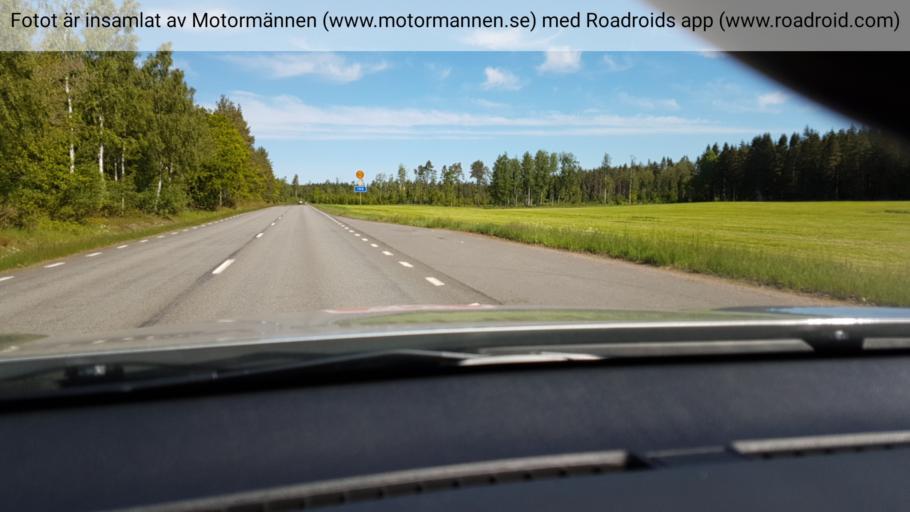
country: SE
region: Vaestra Goetaland
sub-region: Hjo Kommun
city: Hjo
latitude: 58.3829
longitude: 14.3517
